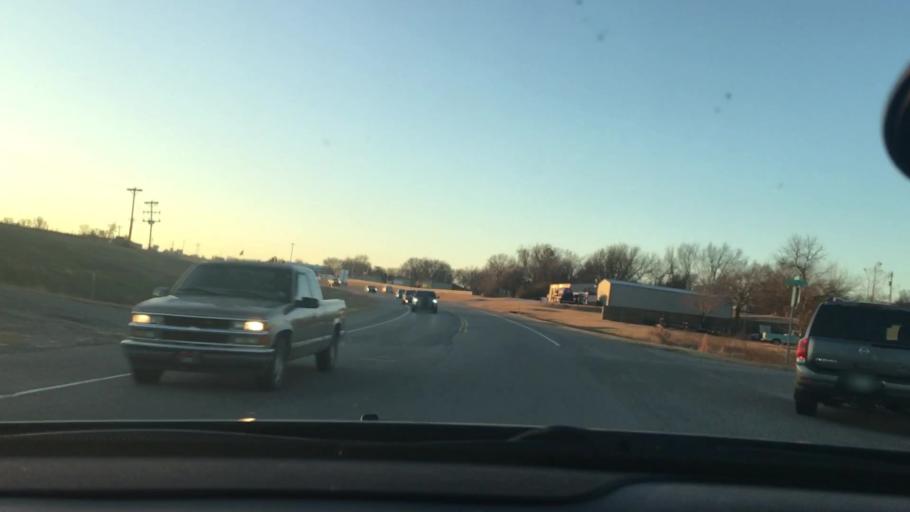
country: US
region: Oklahoma
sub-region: Pontotoc County
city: Ada
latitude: 34.7603
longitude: -96.7036
